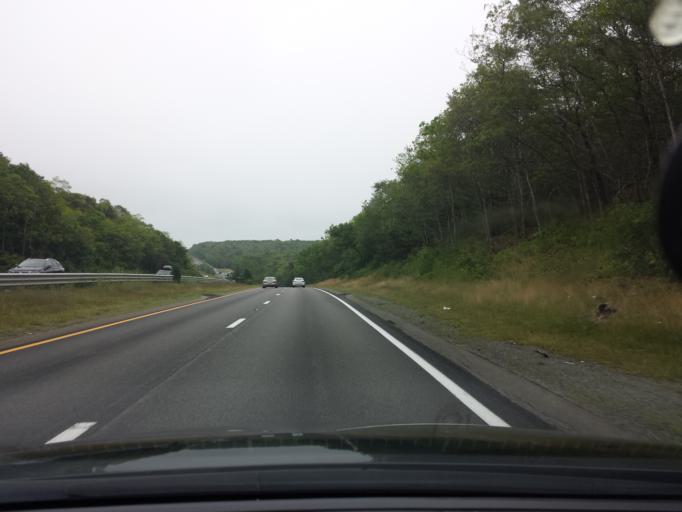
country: US
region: Massachusetts
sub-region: Barnstable County
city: Sandwich
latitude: 41.7400
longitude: -70.5015
